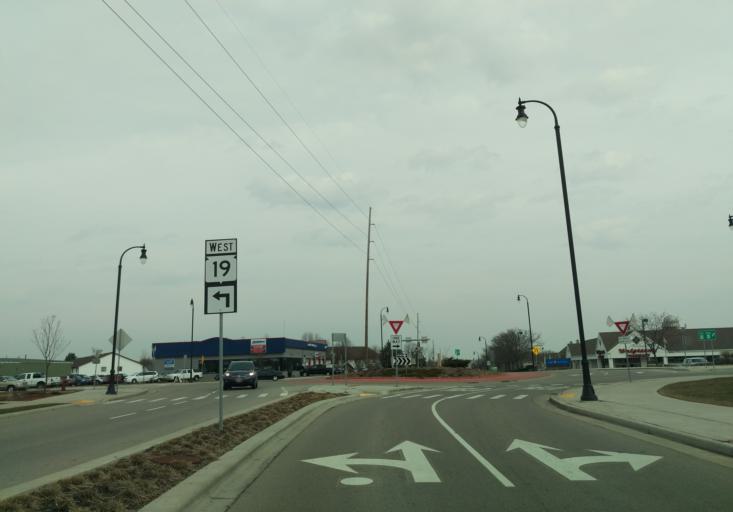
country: US
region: Wisconsin
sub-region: Dane County
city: Waunakee
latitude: 43.1914
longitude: -89.4618
